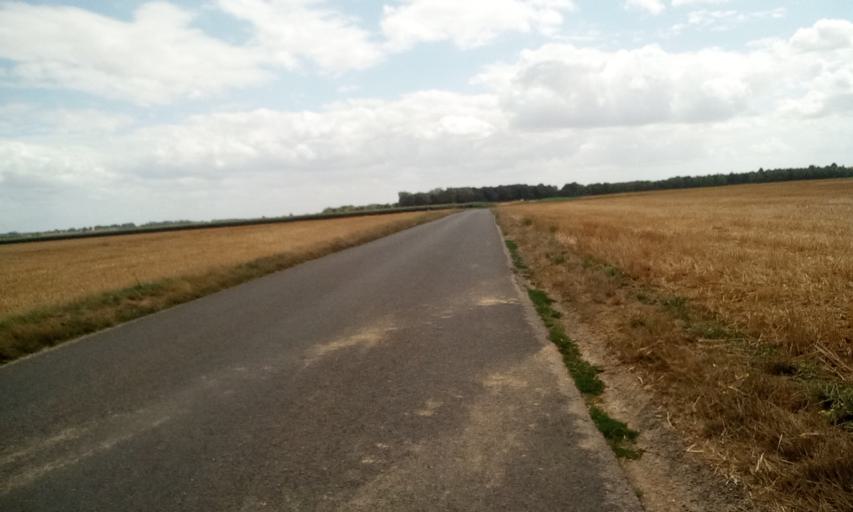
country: FR
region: Lower Normandy
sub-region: Departement du Calvados
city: Creully
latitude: 49.2788
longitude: -0.5332
